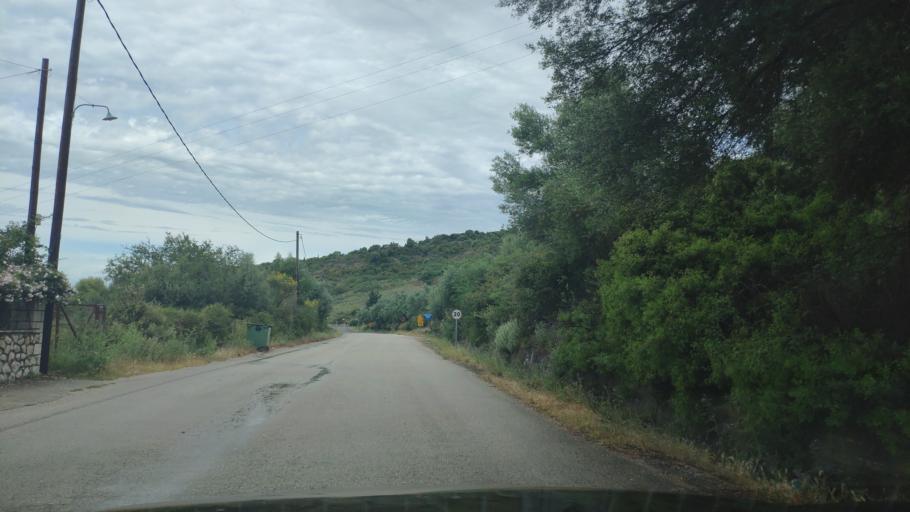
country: GR
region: West Greece
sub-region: Nomos Aitolias kai Akarnanias
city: Palairos
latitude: 38.7555
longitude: 20.8863
